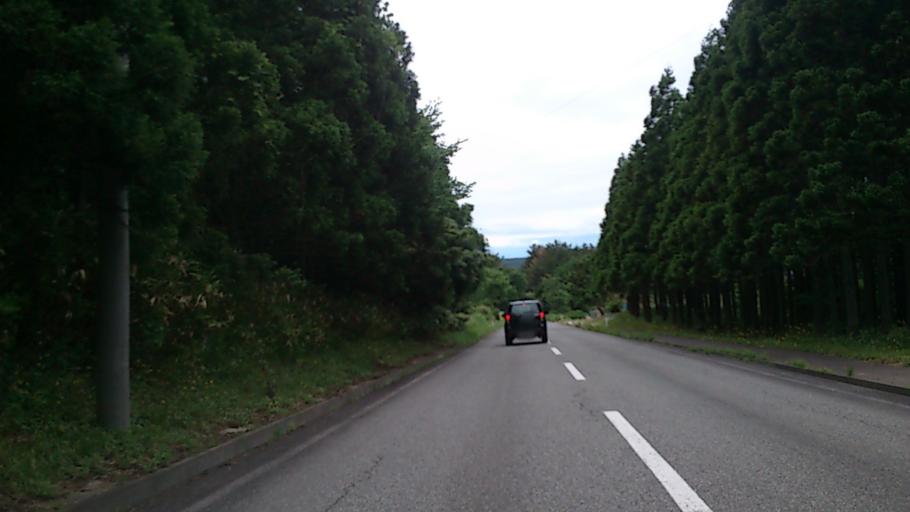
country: JP
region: Yamagata
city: Yuza
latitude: 39.0792
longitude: 139.8752
